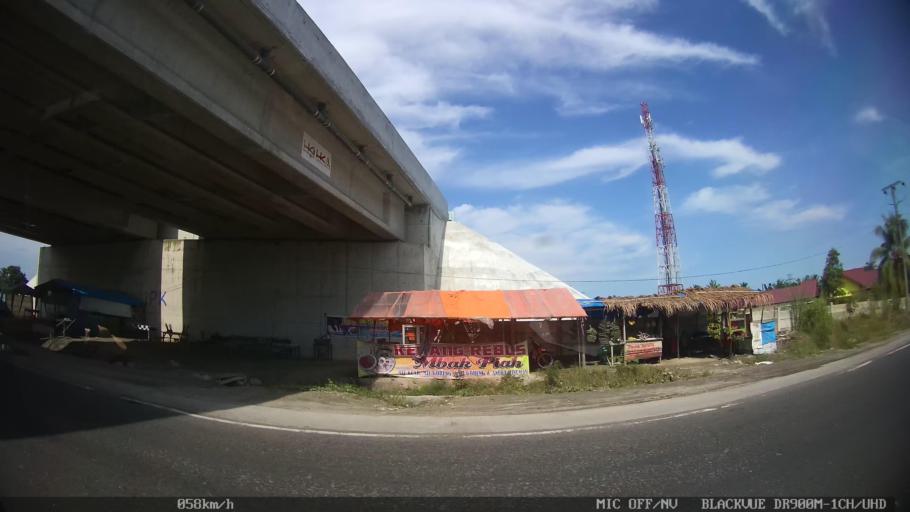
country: ID
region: North Sumatra
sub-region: Kabupaten Langkat
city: Stabat
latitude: 3.7142
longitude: 98.5041
